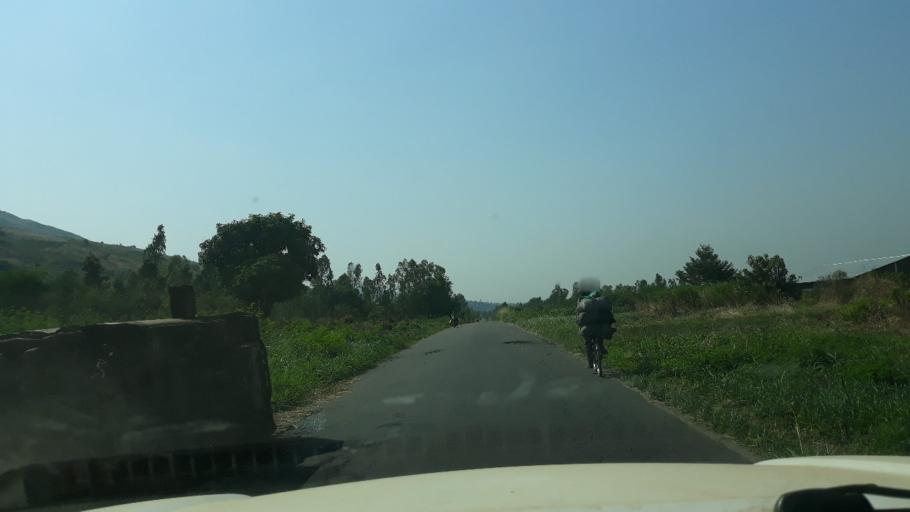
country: CD
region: South Kivu
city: Uvira
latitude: -3.2587
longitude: 29.1612
